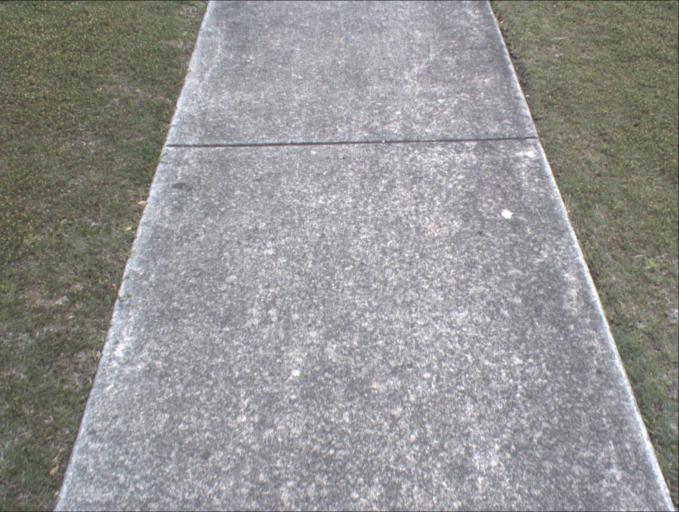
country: AU
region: Queensland
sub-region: Logan
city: Logan Reserve
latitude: -27.6849
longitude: 153.0920
